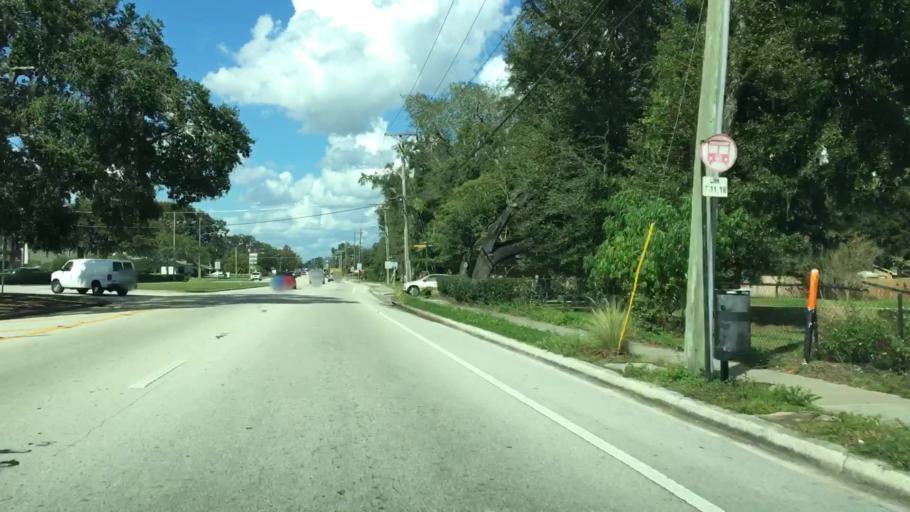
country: US
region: Florida
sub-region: Orange County
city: Edgewood
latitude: 28.4833
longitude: -81.3717
